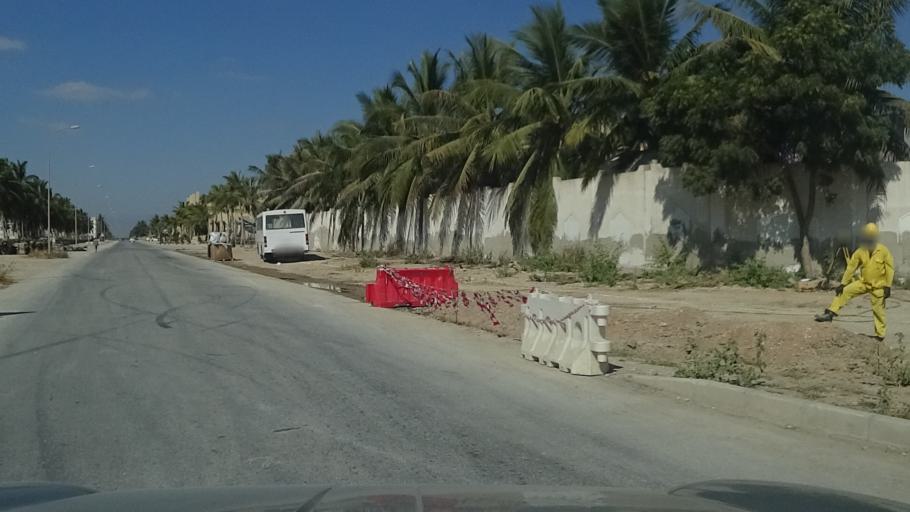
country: OM
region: Zufar
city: Salalah
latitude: 17.0339
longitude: 54.1668
